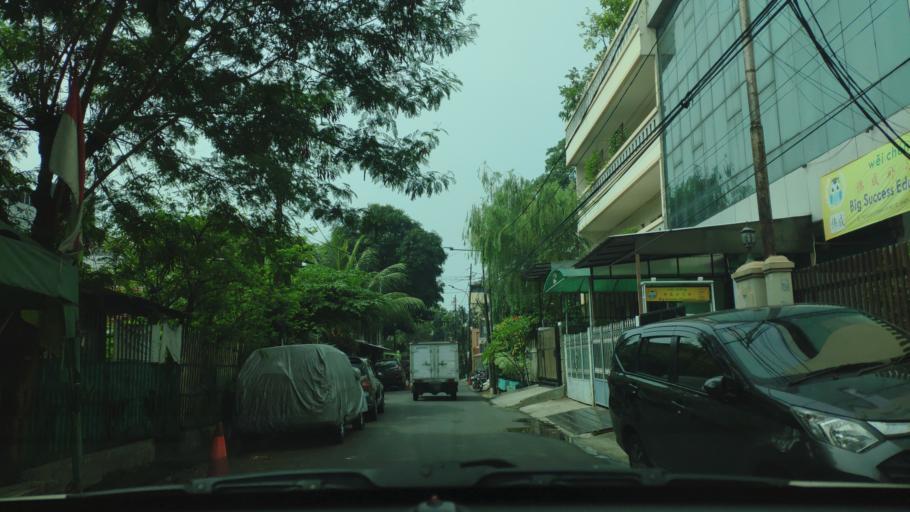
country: ID
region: Jakarta Raya
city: Jakarta
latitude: -6.1638
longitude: 106.8137
